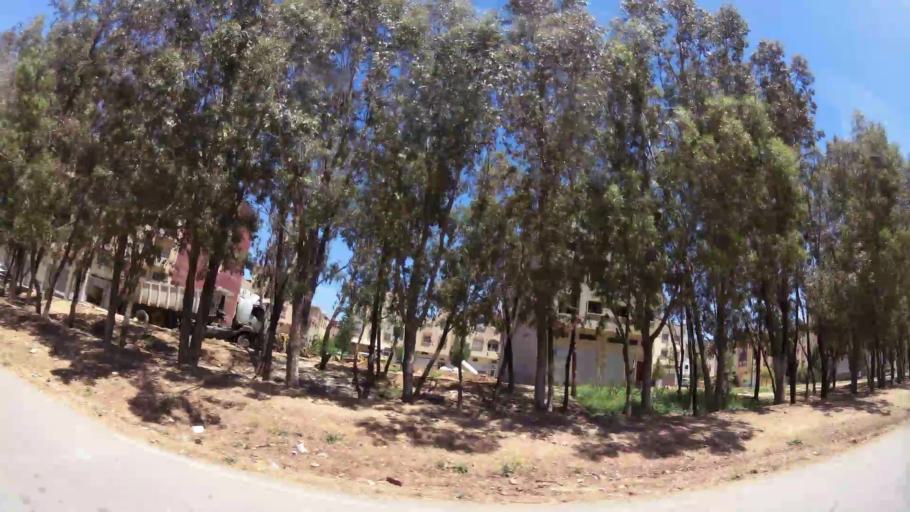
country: MA
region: Meknes-Tafilalet
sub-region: Meknes
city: Meknes
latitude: 33.8498
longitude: -5.5594
